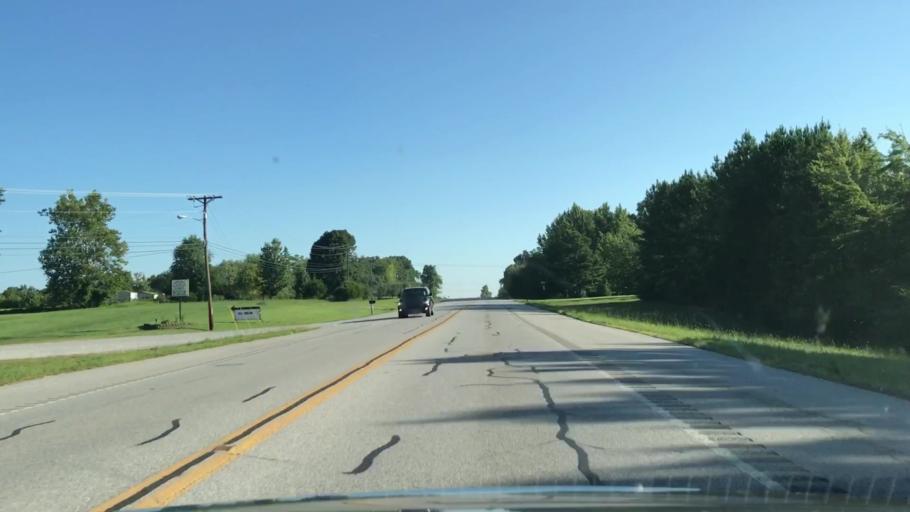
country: US
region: Tennessee
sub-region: Putnam County
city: Baxter
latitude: 36.1765
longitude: -85.6262
